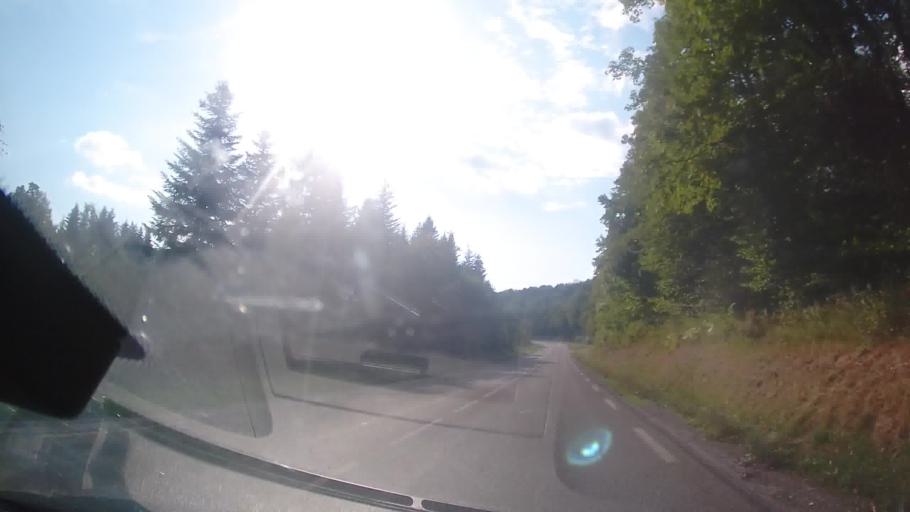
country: FR
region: Franche-Comte
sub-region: Departement du Jura
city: Orgelet
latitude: 46.6002
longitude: 5.6561
